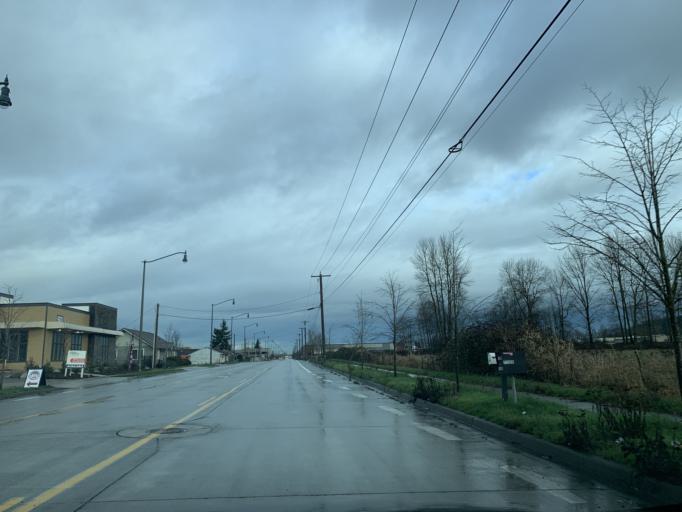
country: US
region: Washington
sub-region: King County
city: Pacific
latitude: 47.2368
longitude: -122.2487
